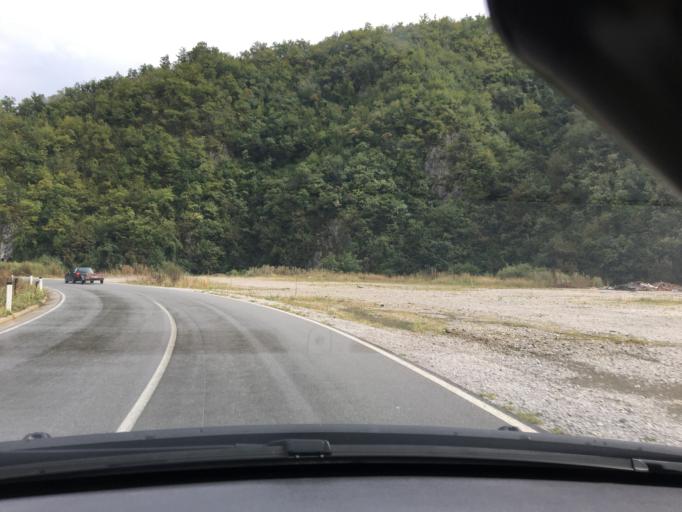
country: ME
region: Berane
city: Berane
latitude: 42.8294
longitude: 19.8336
